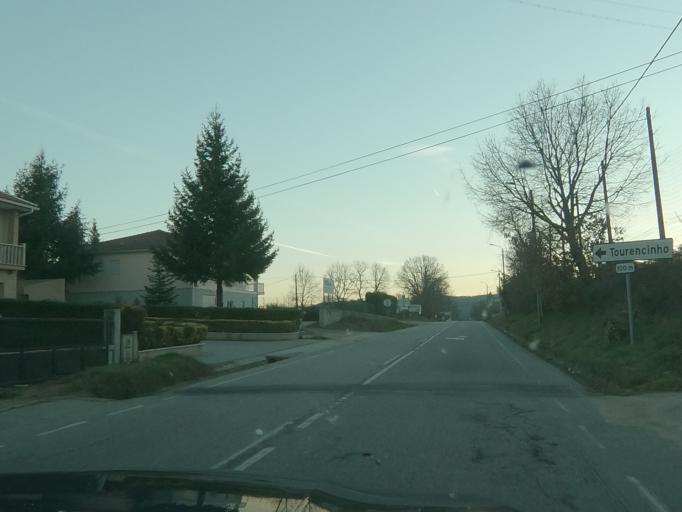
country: PT
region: Vila Real
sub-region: Vila Pouca de Aguiar
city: Vila Pouca de Aguiar
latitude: 41.4319
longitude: -7.6798
